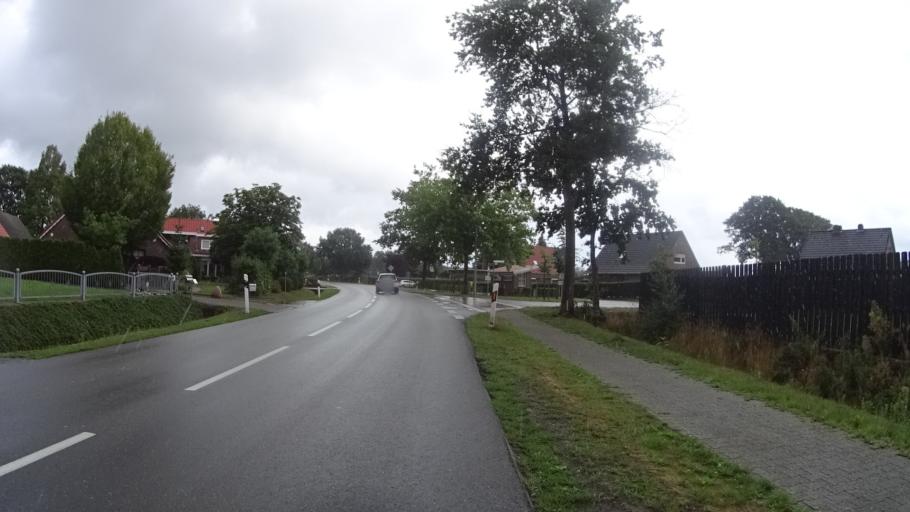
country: DE
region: Lower Saxony
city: Schwerinsdorf
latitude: 53.3423
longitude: 7.7531
